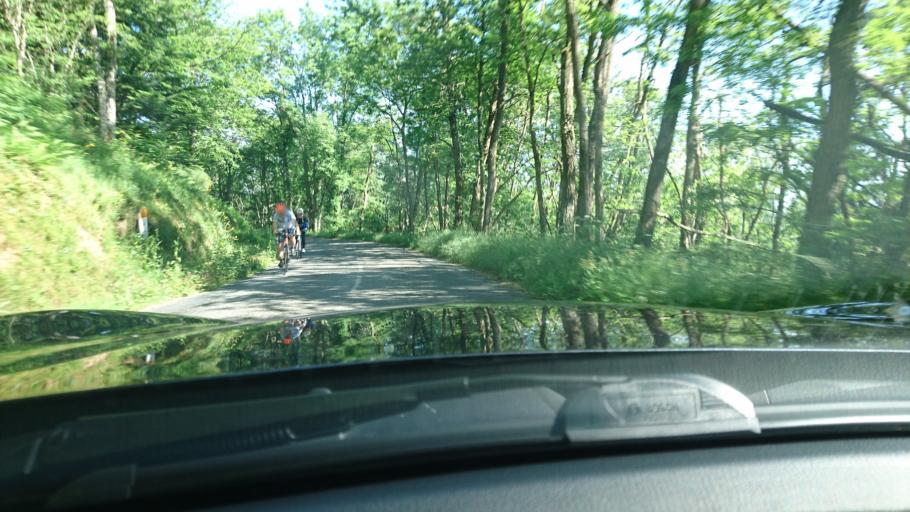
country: FR
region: Rhone-Alpes
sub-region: Departement du Rhone
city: Saint-Pierre-la-Palud
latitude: 45.7644
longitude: 4.6101
